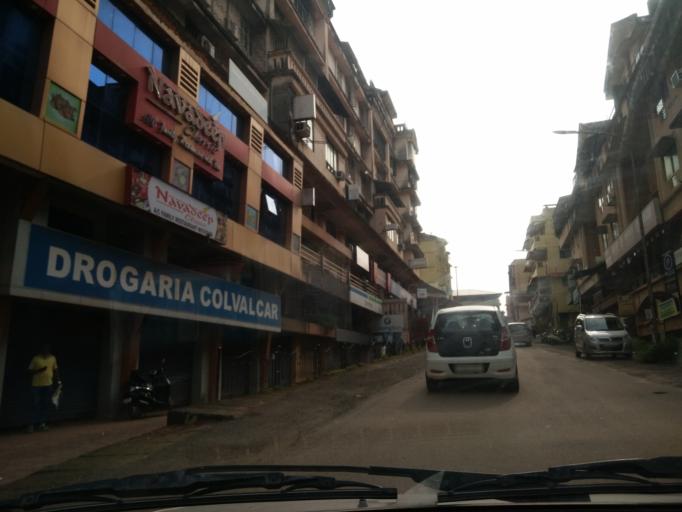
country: IN
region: Goa
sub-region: South Goa
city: Madgaon
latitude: 15.2747
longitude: 73.9549
